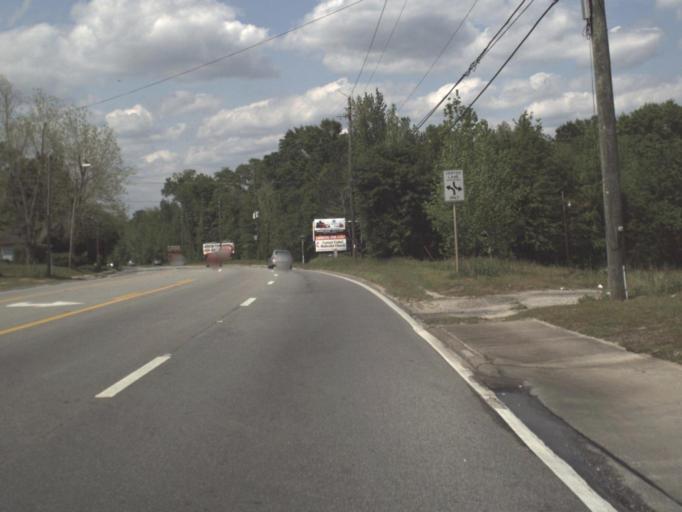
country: US
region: Florida
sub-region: Escambia County
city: Century
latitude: 30.9840
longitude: -87.2566
